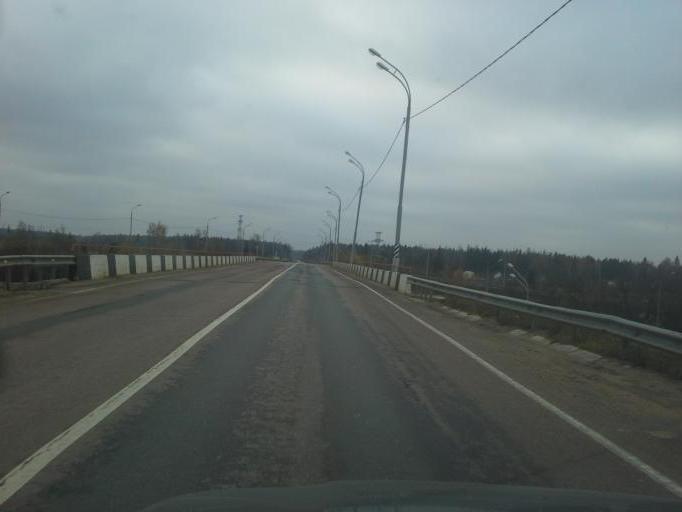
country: RU
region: Moskovskaya
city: Peshki
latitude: 56.1511
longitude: 37.0369
